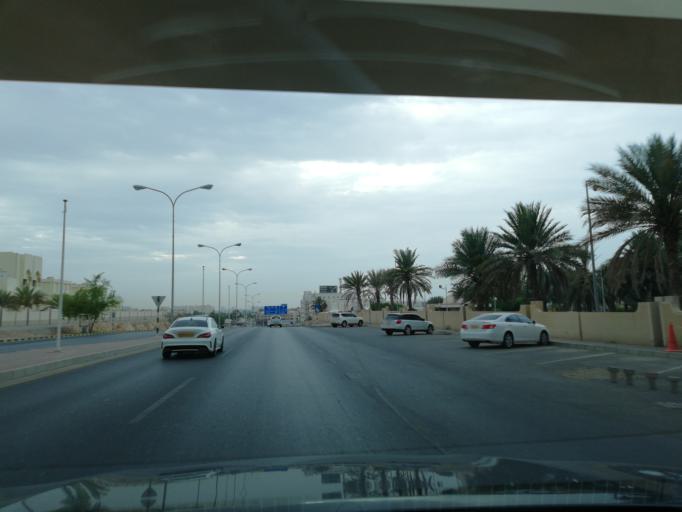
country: OM
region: Muhafazat Masqat
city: Bawshar
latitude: 23.5741
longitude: 58.3873
